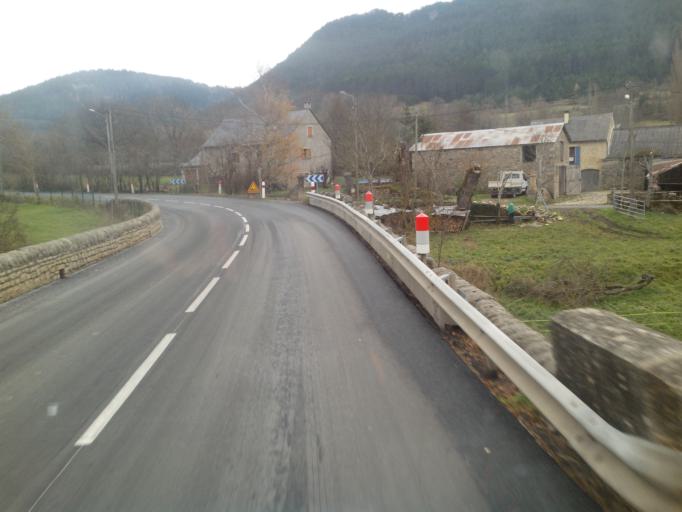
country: FR
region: Languedoc-Roussillon
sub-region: Departement de la Lozere
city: Mende
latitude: 44.4540
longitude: 3.5420
